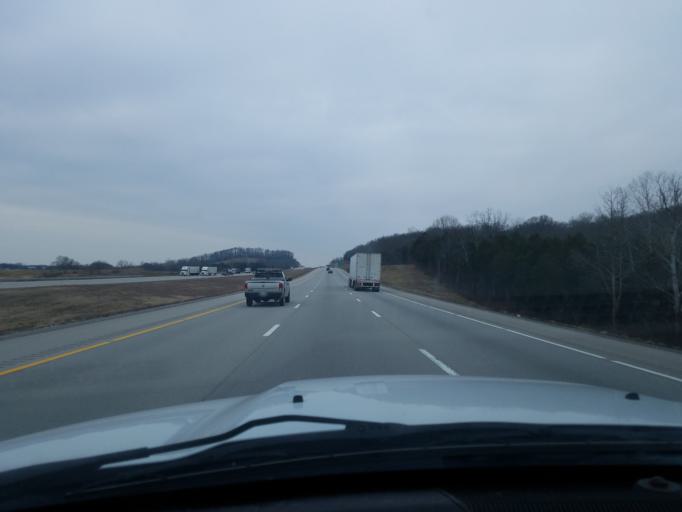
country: US
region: Kentucky
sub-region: Barren County
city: Cave City
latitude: 37.1132
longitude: -86.0287
